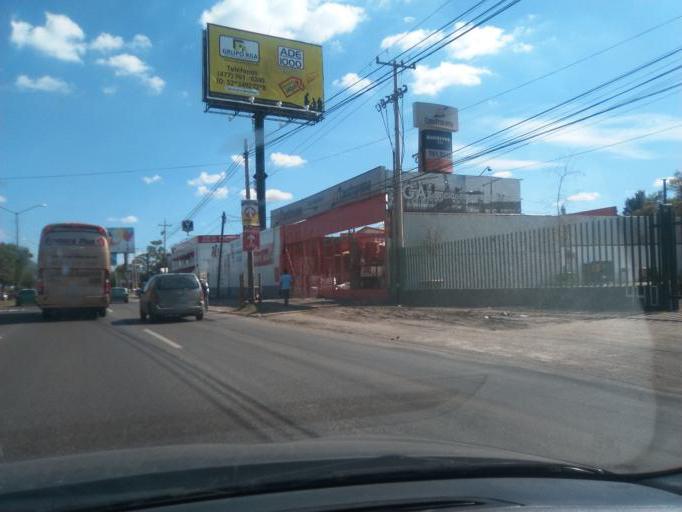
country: MX
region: Guanajuato
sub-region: Leon
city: Fraccionamiento Paraiso Real
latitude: 21.0868
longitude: -101.6164
